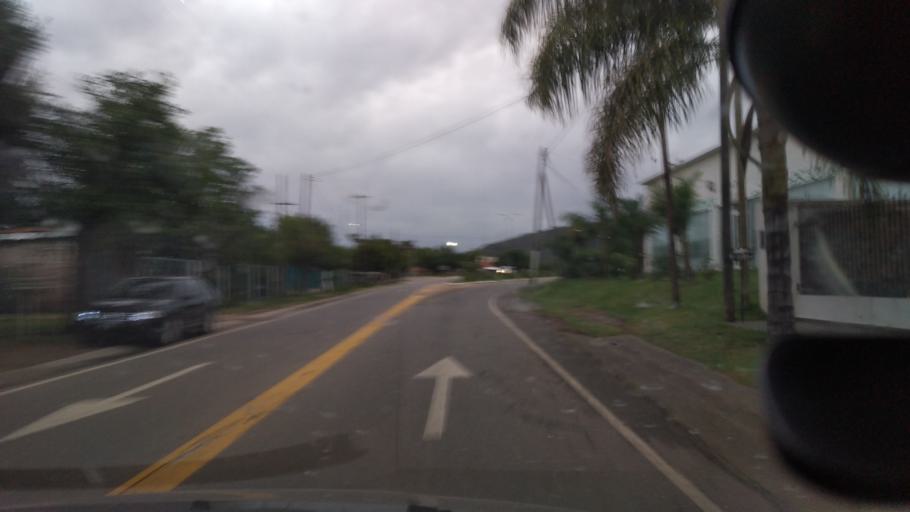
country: AR
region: Cordoba
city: Villa Las Rosas
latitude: -31.9134
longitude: -65.0354
